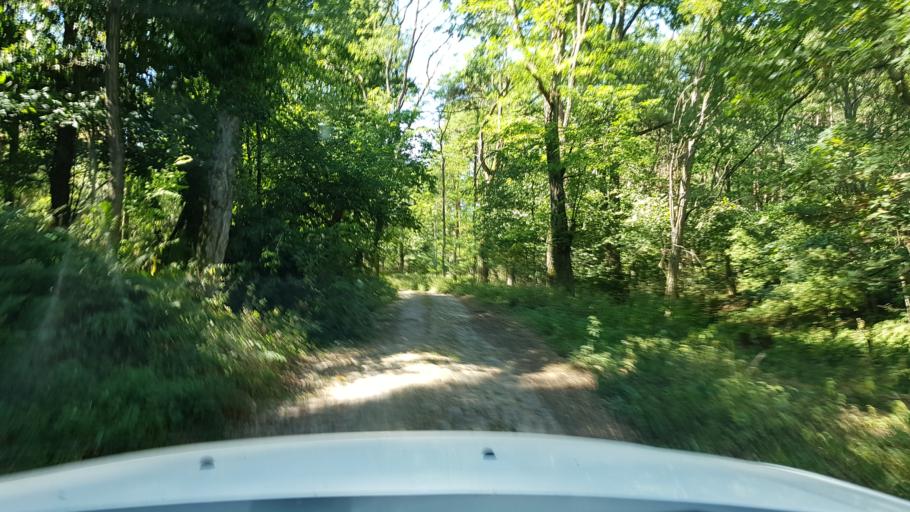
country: PL
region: West Pomeranian Voivodeship
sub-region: Powiat gryfinski
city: Cedynia
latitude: 52.8495
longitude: 14.2315
